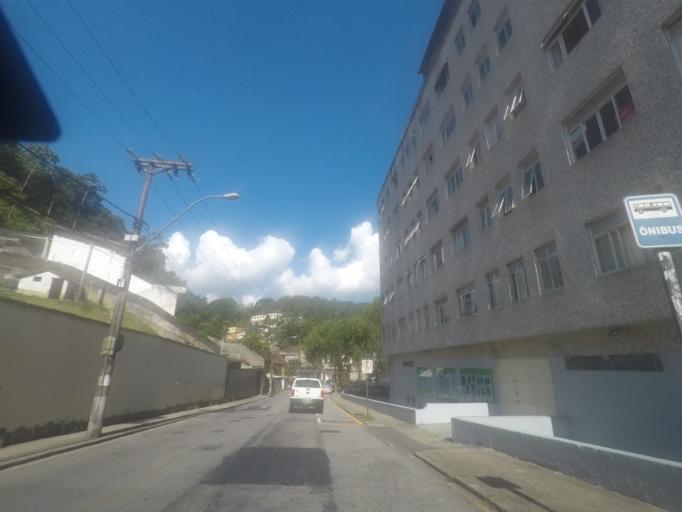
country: BR
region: Rio de Janeiro
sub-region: Petropolis
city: Petropolis
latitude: -22.5207
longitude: -43.1894
